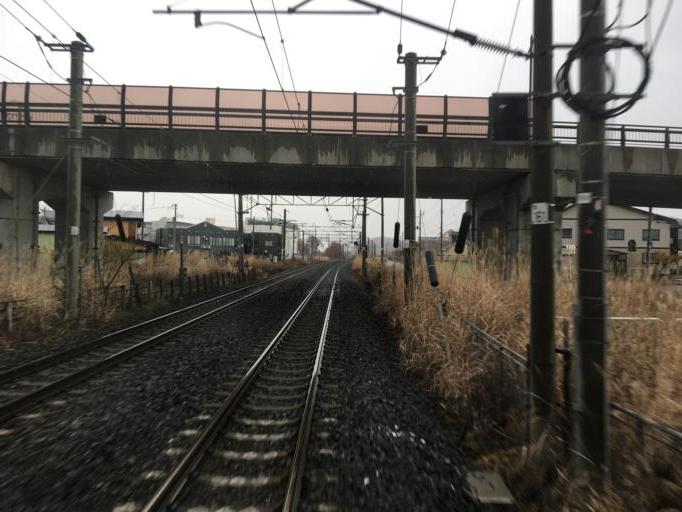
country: JP
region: Aomori
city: Aomori Shi
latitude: 40.8162
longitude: 140.7941
